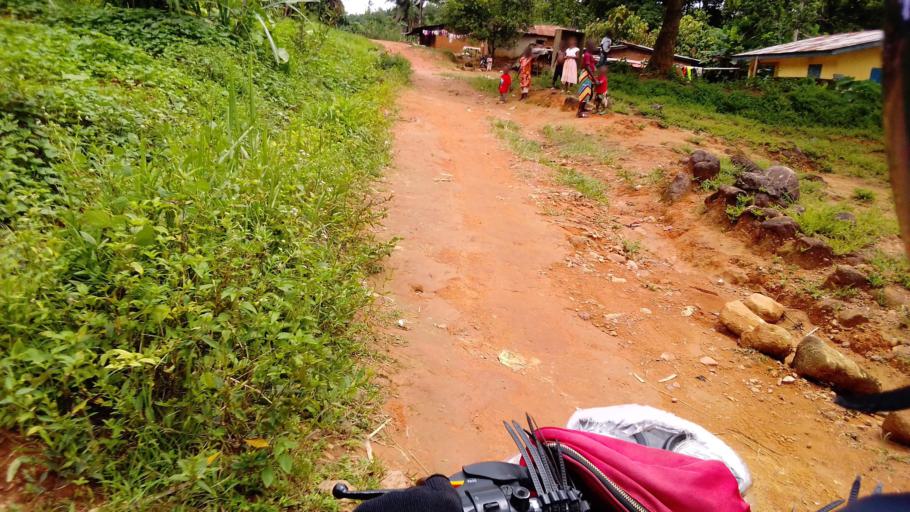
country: SL
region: Eastern Province
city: Koyima
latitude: 8.6789
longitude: -11.0069
